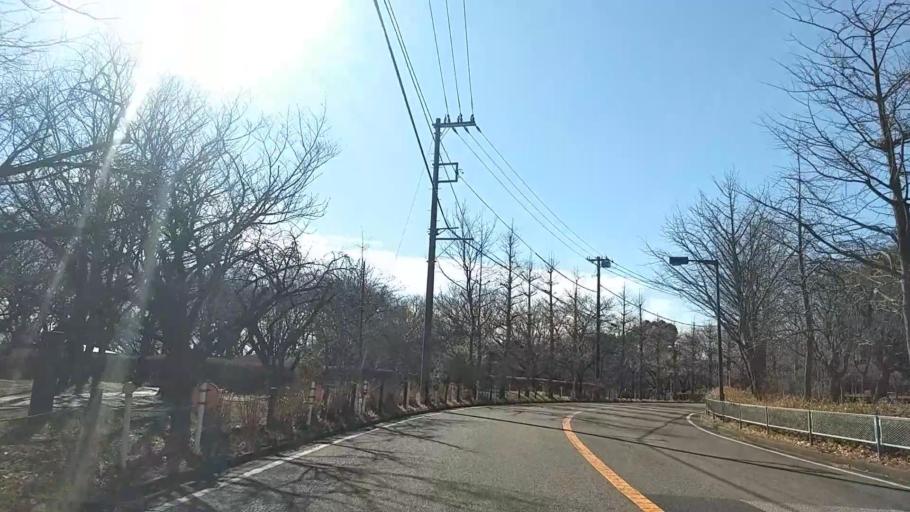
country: JP
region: Kanagawa
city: Yokohama
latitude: 35.4553
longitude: 139.5879
